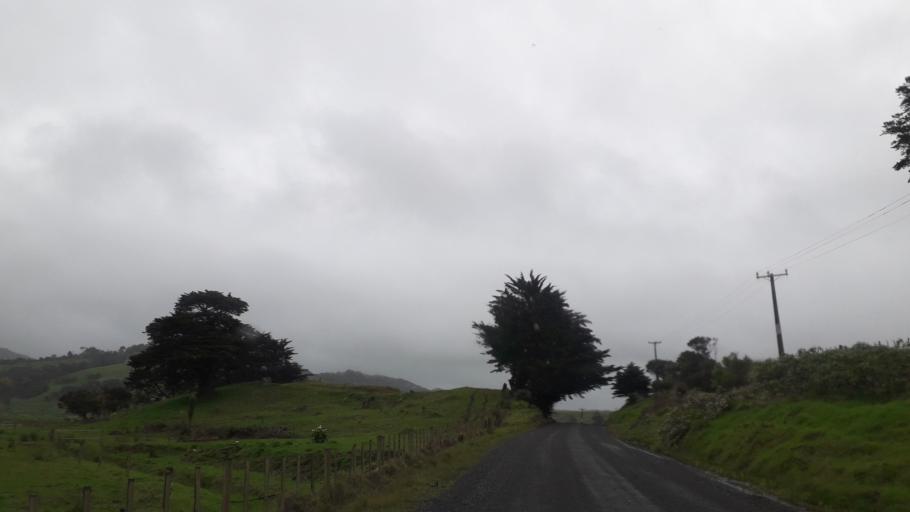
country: NZ
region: Northland
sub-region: Far North District
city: Ahipara
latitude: -35.4186
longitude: 173.3625
